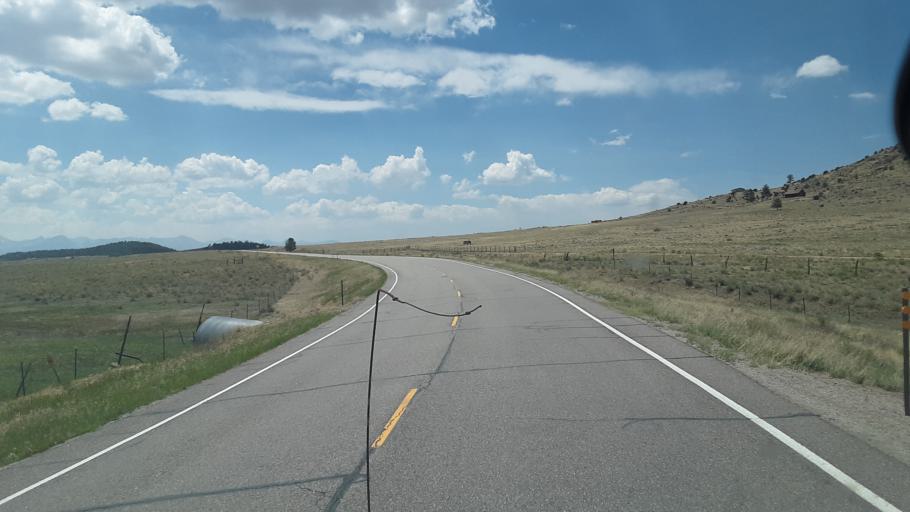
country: US
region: Colorado
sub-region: Custer County
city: Westcliffe
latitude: 38.1644
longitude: -105.2726
